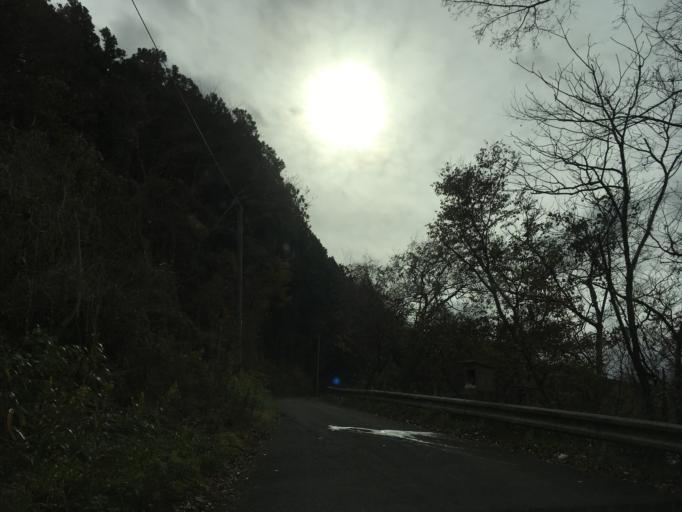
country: JP
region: Iwate
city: Ichinoseki
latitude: 38.7870
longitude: 141.2647
